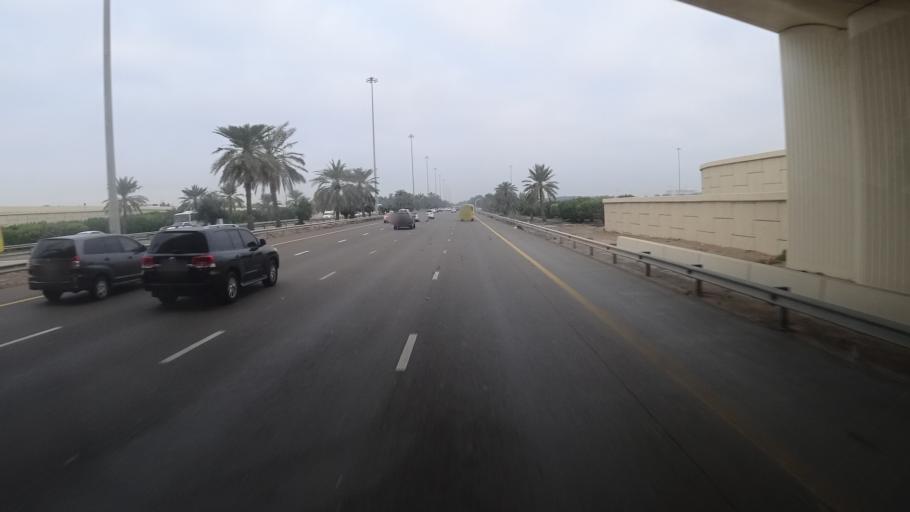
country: AE
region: Abu Dhabi
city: Abu Dhabi
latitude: 24.3522
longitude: 54.5694
